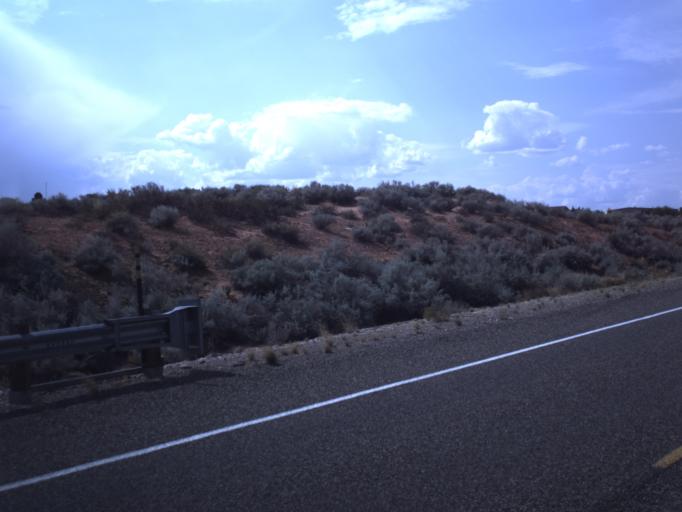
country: US
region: Arizona
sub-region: Coconino County
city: Page
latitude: 37.0573
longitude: -111.6390
